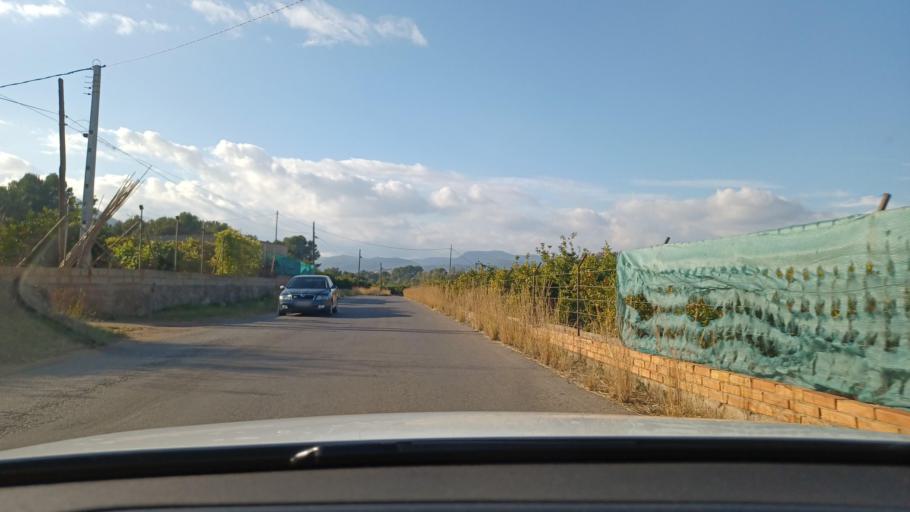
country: ES
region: Valencia
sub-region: Provincia de Castello
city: Onda
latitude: 39.9561
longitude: -0.2440
